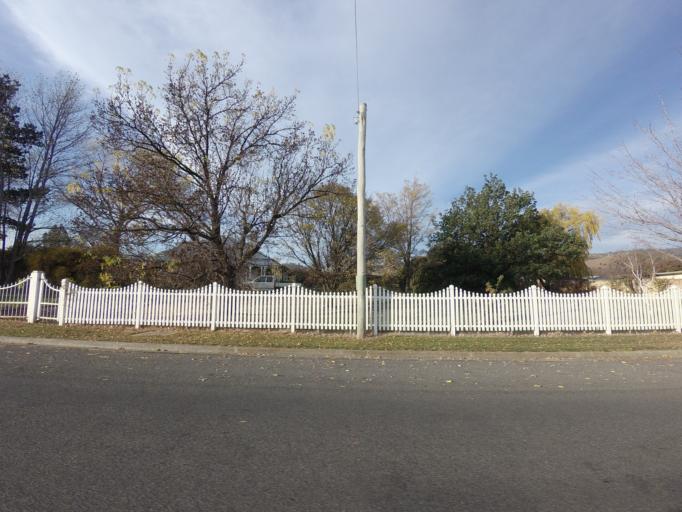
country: AU
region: Tasmania
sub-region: Brighton
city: Bridgewater
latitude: -42.5337
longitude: 147.2022
